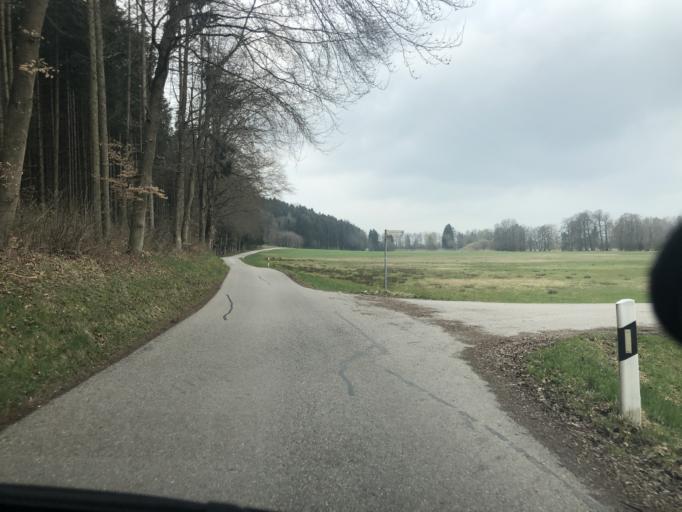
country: DE
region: Bavaria
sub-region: Upper Bavaria
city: Zolling
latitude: 48.4389
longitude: 11.7538
